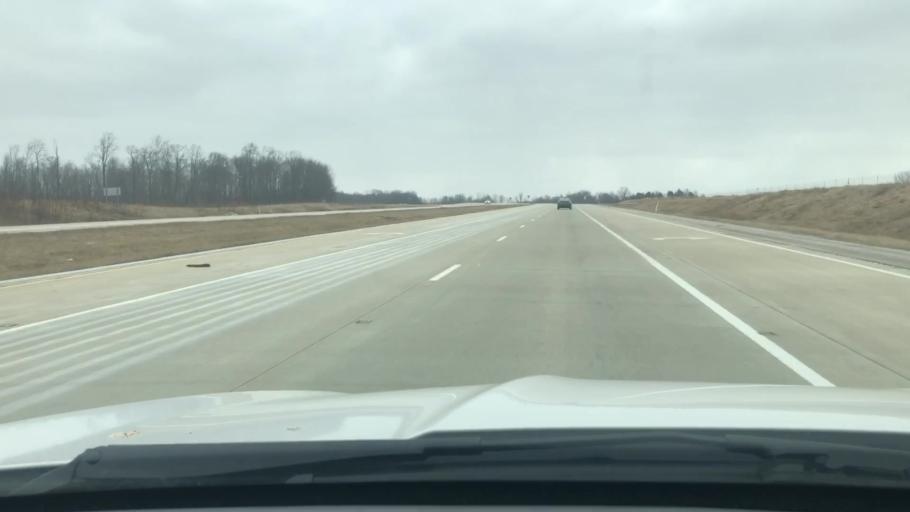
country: US
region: Indiana
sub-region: Carroll County
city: Delphi
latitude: 40.5161
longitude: -86.7215
